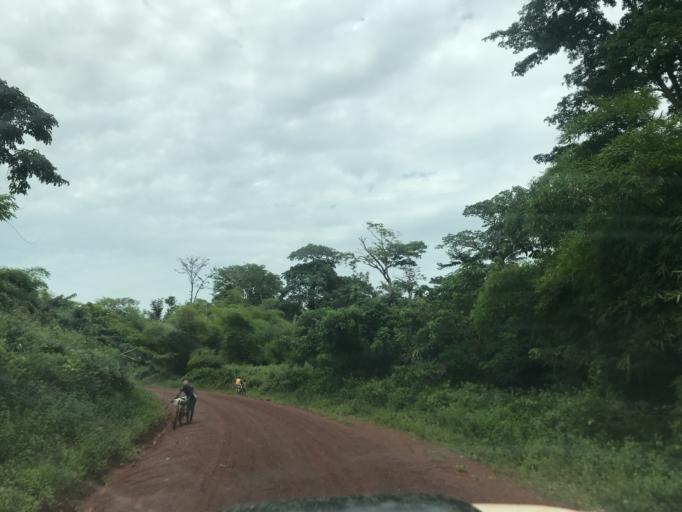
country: CD
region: Eastern Province
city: Buta
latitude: 2.3502
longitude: 24.9530
